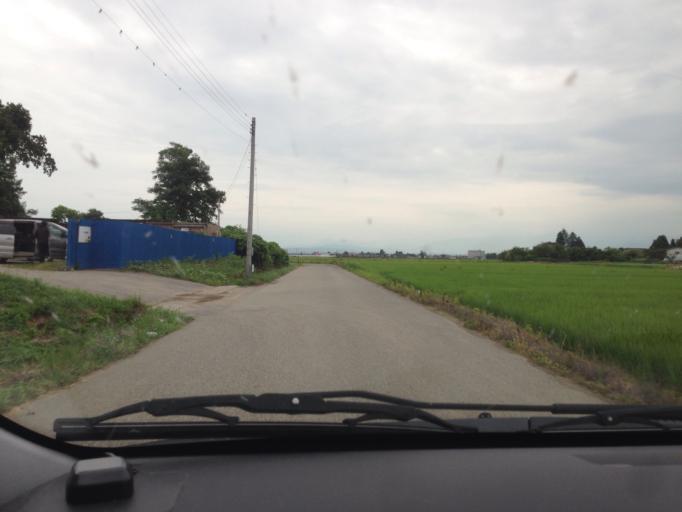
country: JP
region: Fukushima
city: Kitakata
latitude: 37.5113
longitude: 139.8941
